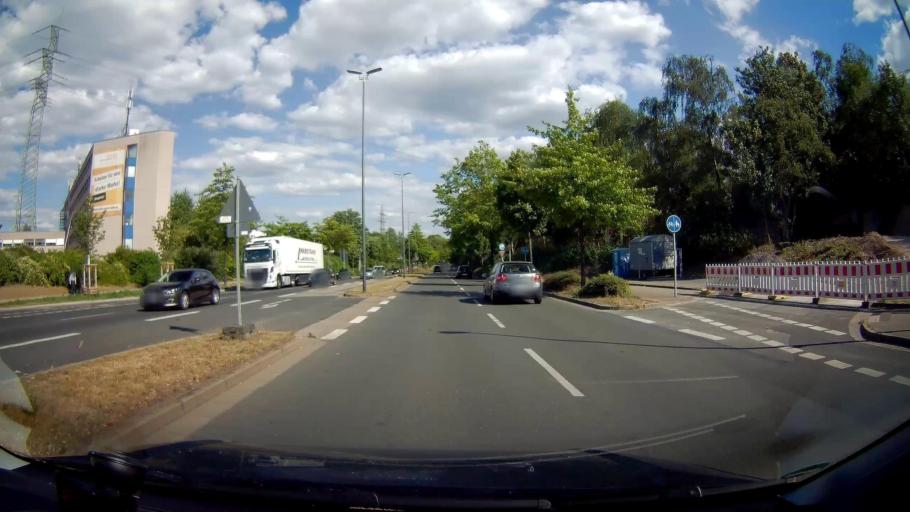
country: DE
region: North Rhine-Westphalia
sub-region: Regierungsbezirk Dusseldorf
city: Essen
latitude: 51.4719
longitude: 6.9920
